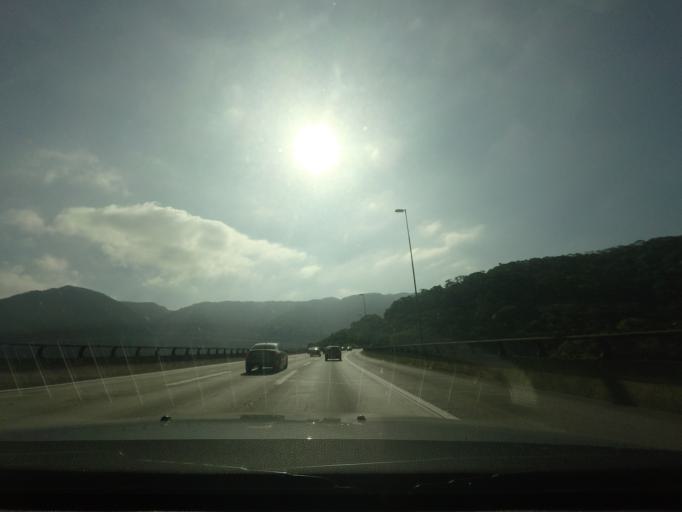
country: BR
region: Sao Paulo
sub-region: Cubatao
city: Cubatao
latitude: -23.8988
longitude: -46.4908
